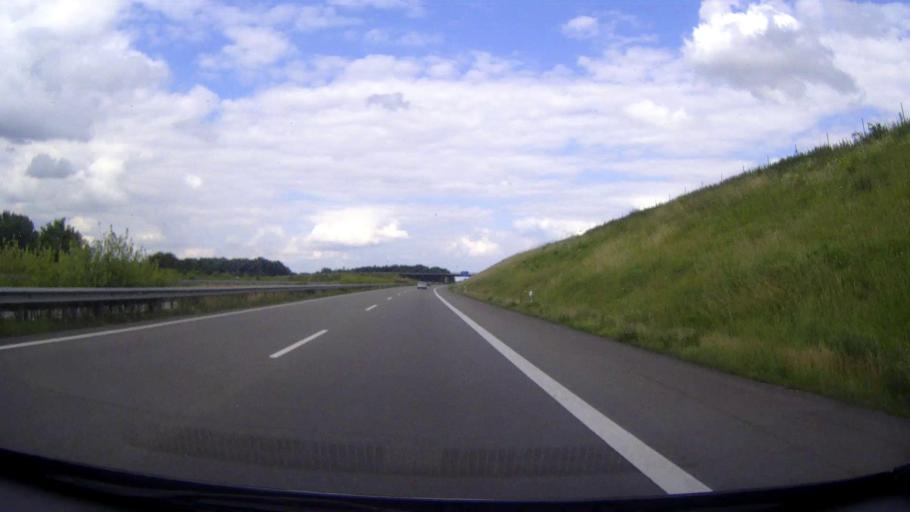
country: DE
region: Schleswig-Holstein
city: Geschendorf
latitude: 53.9226
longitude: 10.4314
